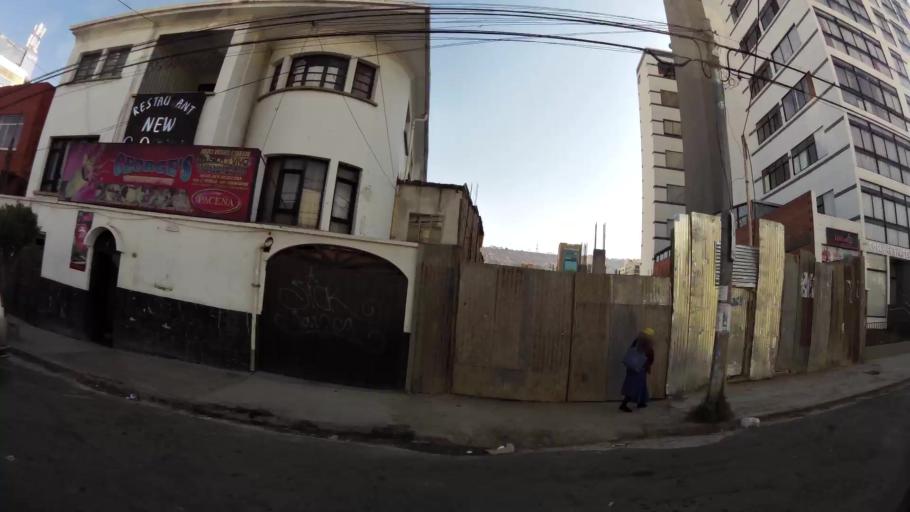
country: BO
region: La Paz
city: La Paz
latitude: -16.5120
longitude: -68.1180
